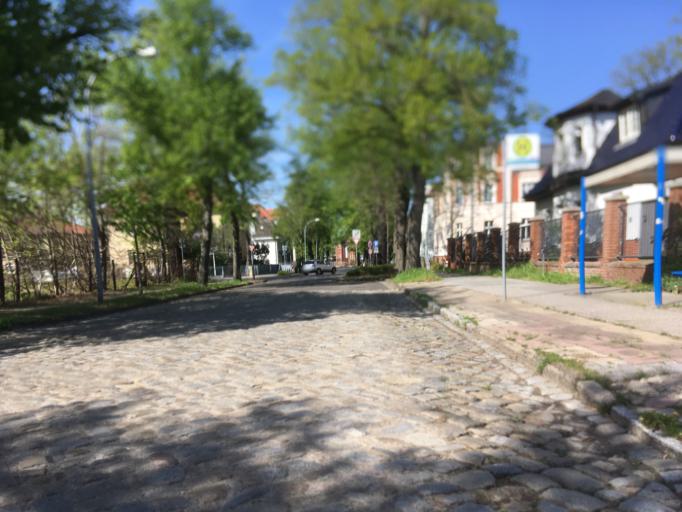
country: DE
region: Brandenburg
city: Konigs Wusterhausen
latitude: 52.2944
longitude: 13.6304
